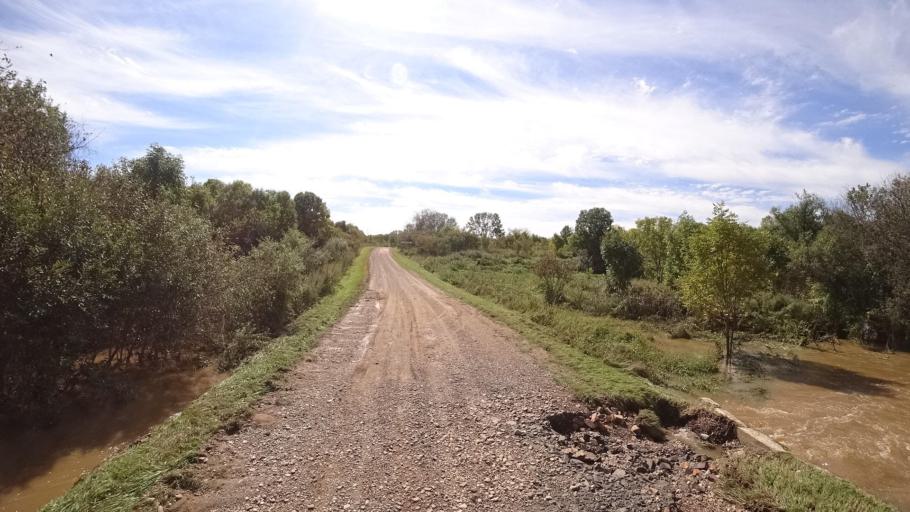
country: RU
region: Primorskiy
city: Kirovskiy
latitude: 44.7612
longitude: 133.6108
